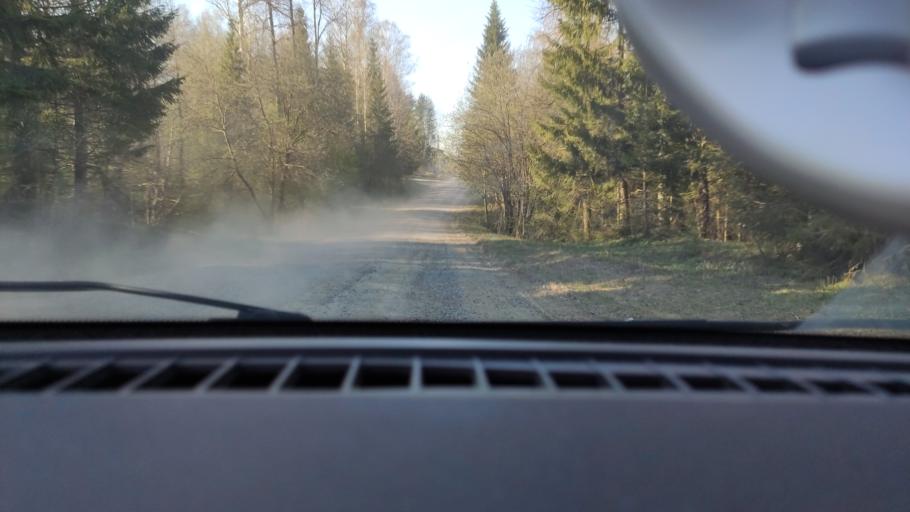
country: RU
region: Perm
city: Polazna
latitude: 58.1336
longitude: 56.4577
